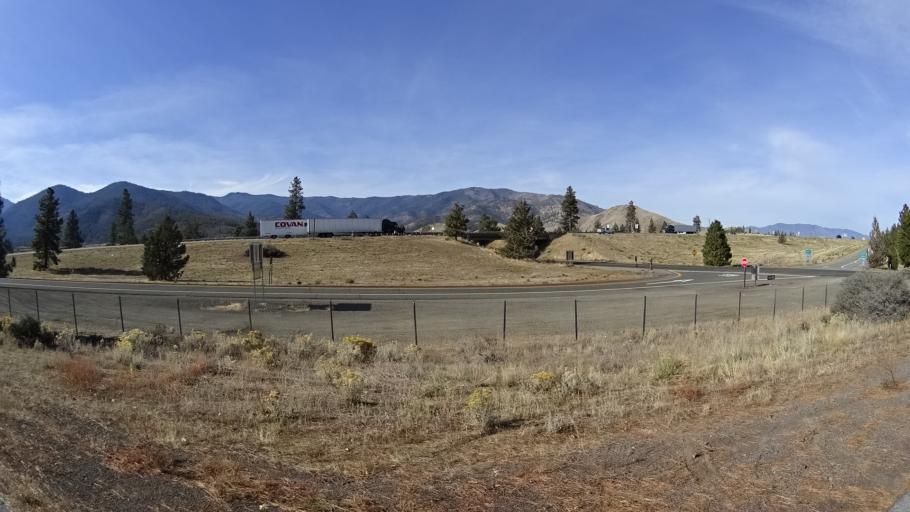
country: US
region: California
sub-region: Siskiyou County
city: Weed
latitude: 41.4420
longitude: -122.4337
